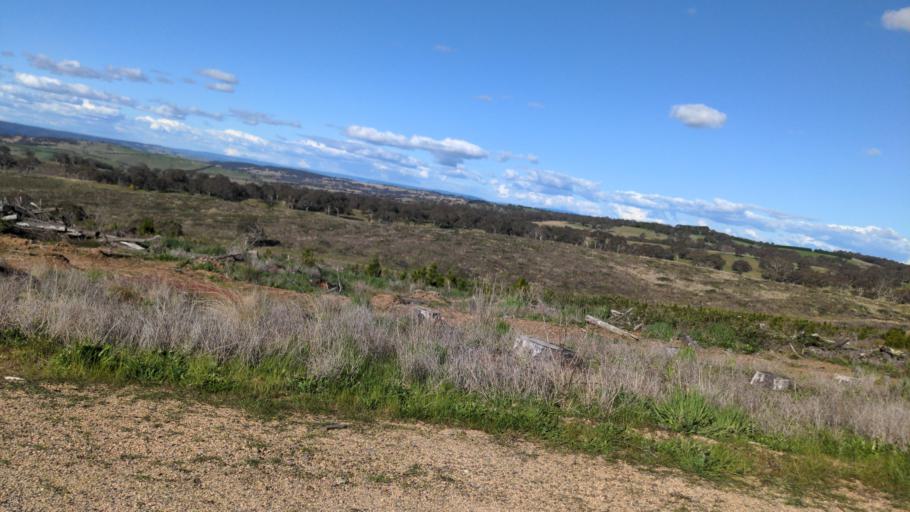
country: AU
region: New South Wales
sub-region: Blayney
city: Blayney
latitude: -33.4248
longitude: 149.3141
